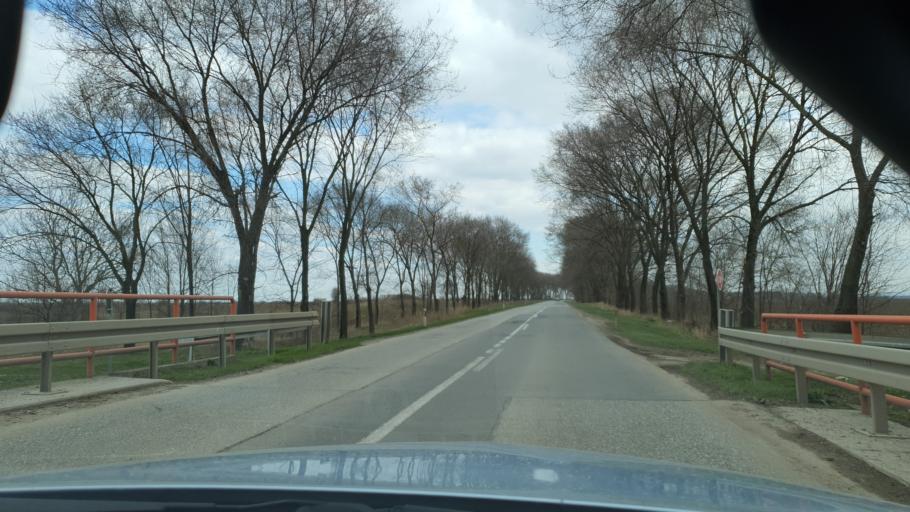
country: RS
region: Autonomna Pokrajina Vojvodina
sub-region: Zapadnobacki Okrug
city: Odzaci
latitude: 45.4489
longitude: 19.3539
